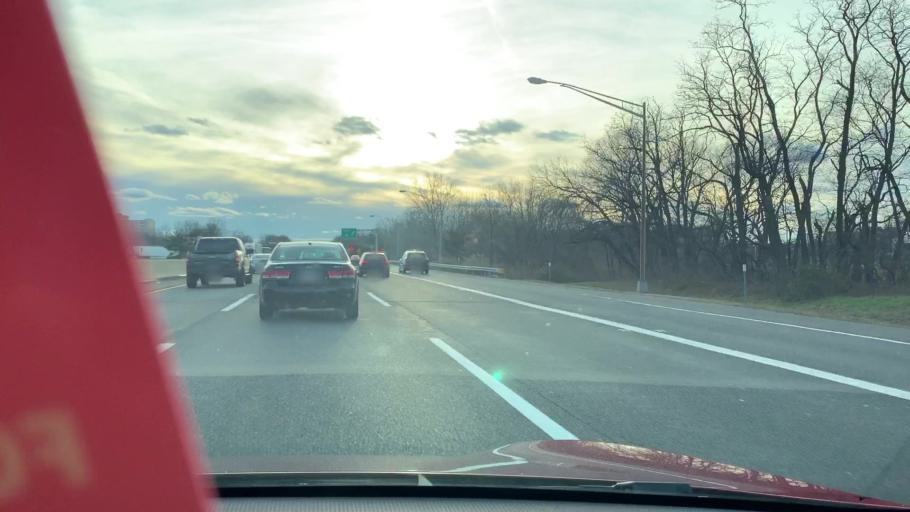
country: US
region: New Jersey
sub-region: Burlington County
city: Ramblewood
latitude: 39.9339
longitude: -74.9499
